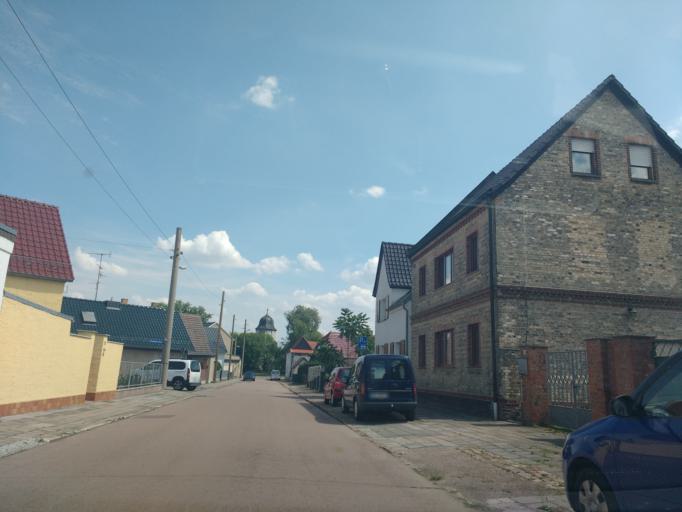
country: DE
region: Saxony-Anhalt
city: Dieskau
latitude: 51.4579
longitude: 12.0352
